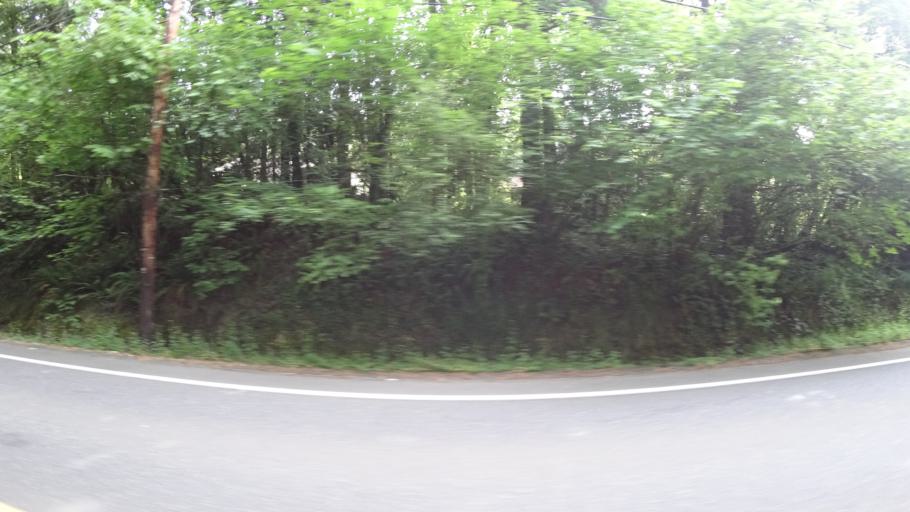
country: US
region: Oregon
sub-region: Clackamas County
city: Lake Oswego
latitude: 45.4447
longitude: -122.6745
